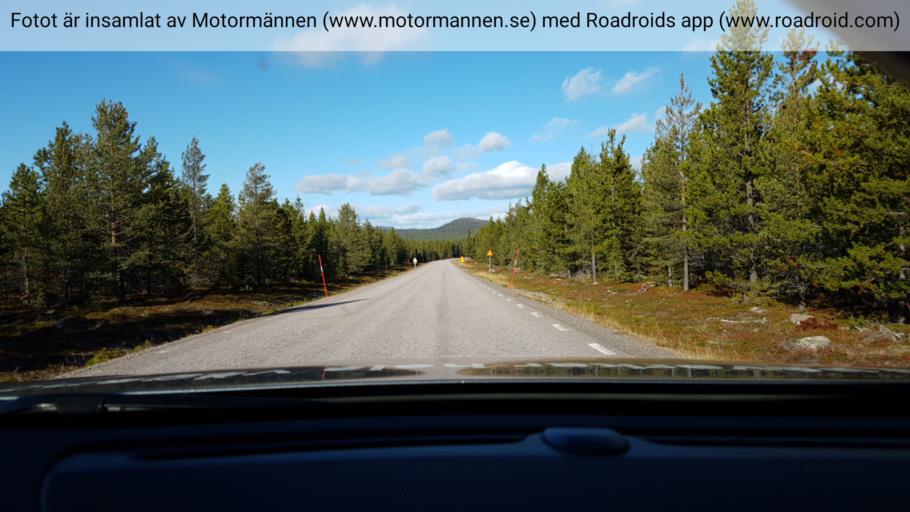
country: SE
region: Norrbotten
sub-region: Arjeplogs Kommun
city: Arjeplog
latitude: 65.8446
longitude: 18.4112
